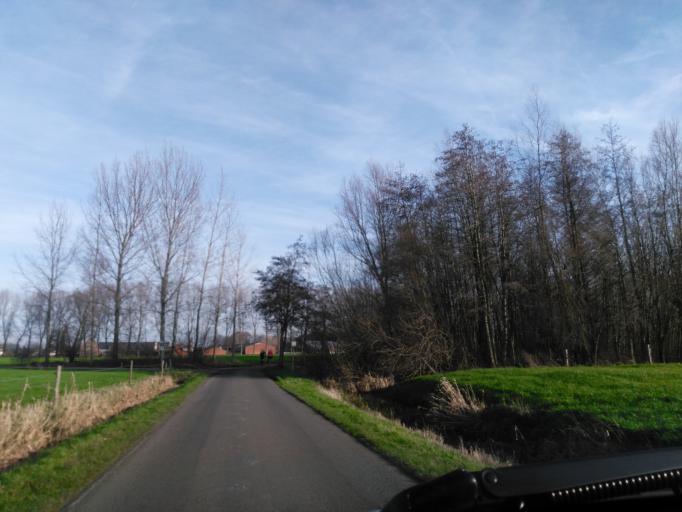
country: BE
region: Flanders
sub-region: Provincie Oost-Vlaanderen
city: Sint-Gillis-Waas
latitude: 51.2190
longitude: 4.1641
